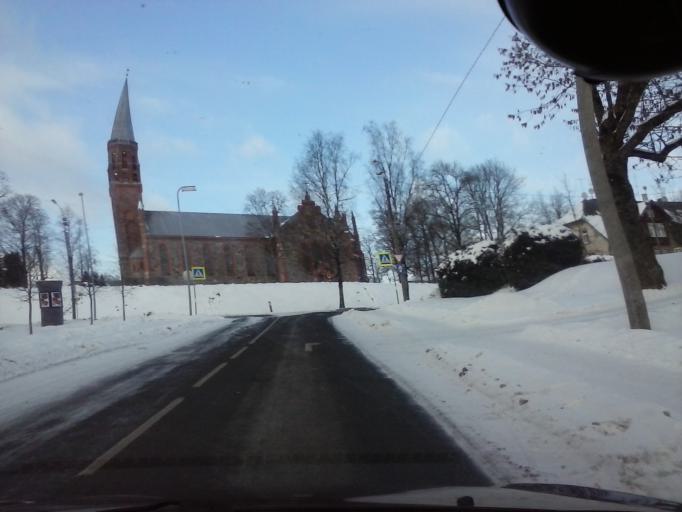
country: EE
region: Viljandimaa
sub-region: Viljandi linn
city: Viljandi
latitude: 58.3627
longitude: 25.5919
